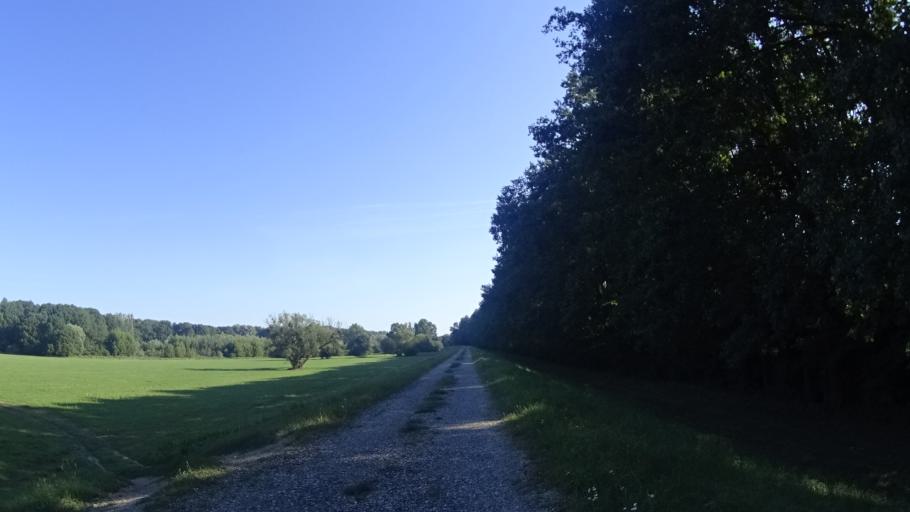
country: CZ
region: South Moravian
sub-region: Okres Breclav
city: Lanzhot
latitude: 48.6642
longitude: 16.9806
